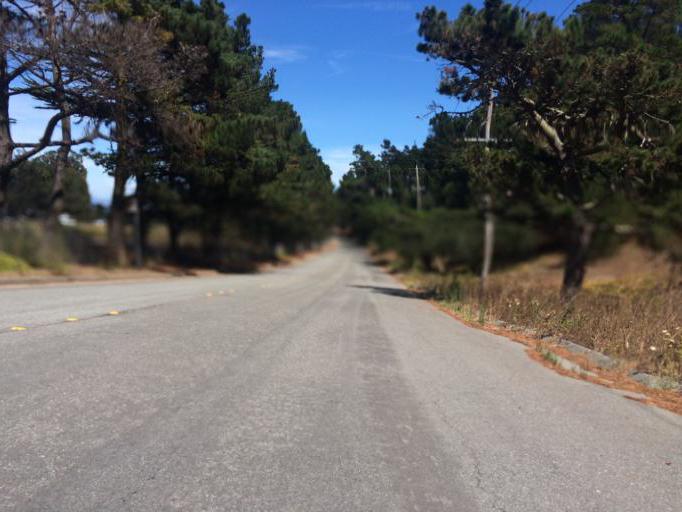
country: US
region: California
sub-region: Monterey County
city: Monterey
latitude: 36.5787
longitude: -121.9060
